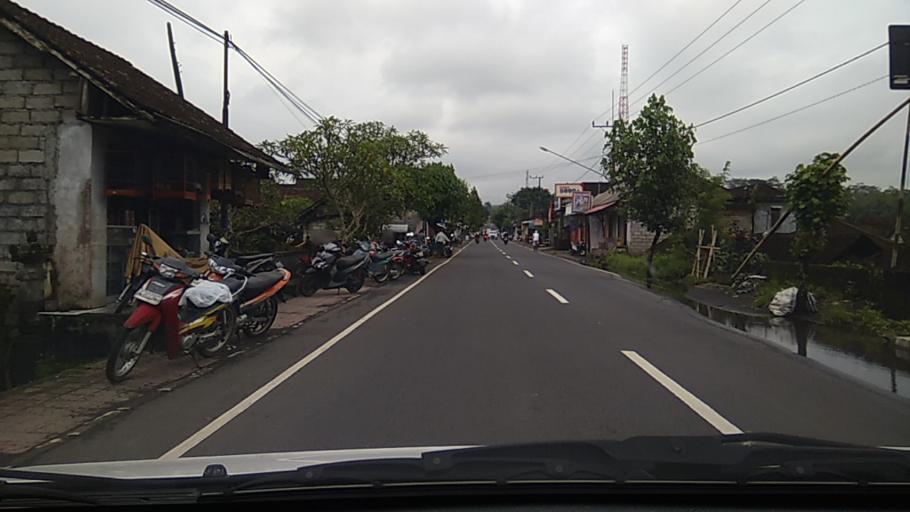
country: ID
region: Bali
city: Banjar Manukayaanyar
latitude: -8.4214
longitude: 115.3088
